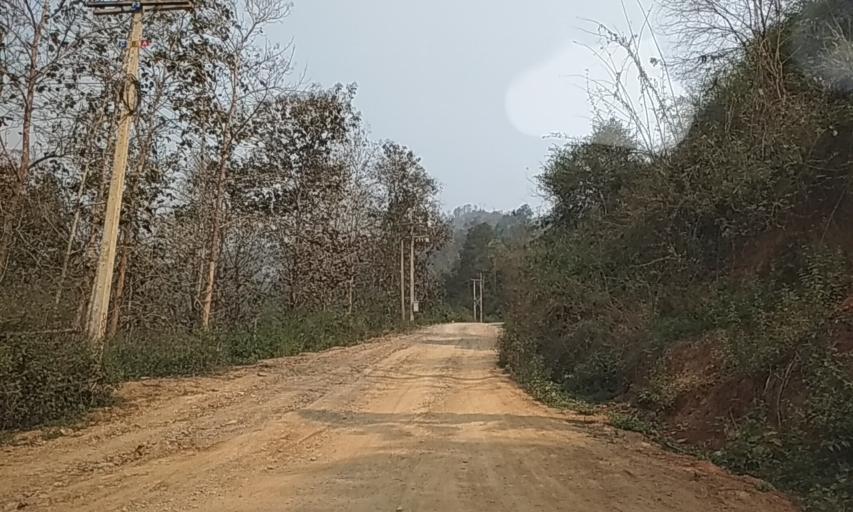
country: TH
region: Nan
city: Chaloem Phra Kiat
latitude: 19.9189
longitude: 101.1621
